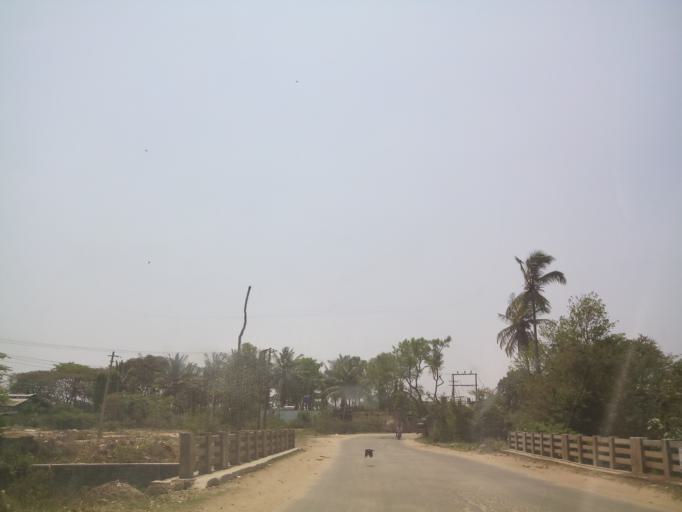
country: IN
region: Karnataka
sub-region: Hassan
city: Hassan
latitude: 12.9924
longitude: 76.0938
